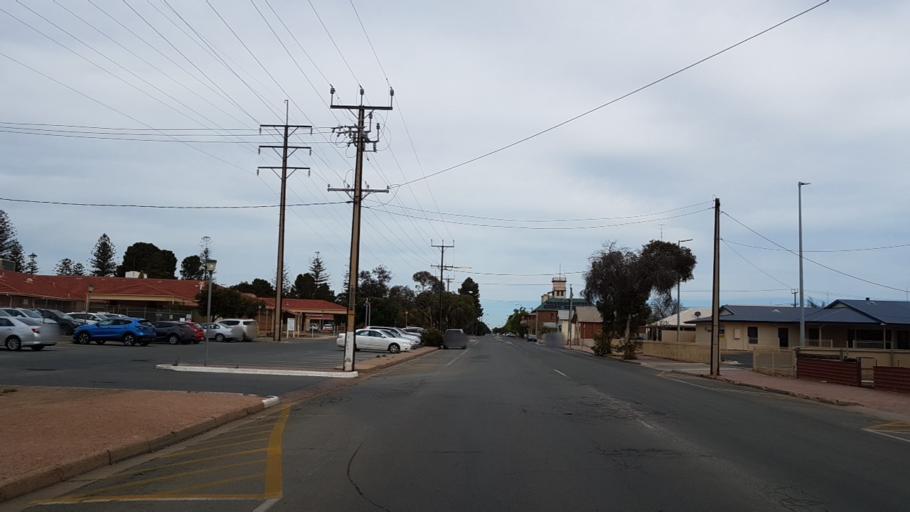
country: AU
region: South Australia
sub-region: Port Pirie City and Dists
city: Port Pirie
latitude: -33.1762
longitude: 138.0039
